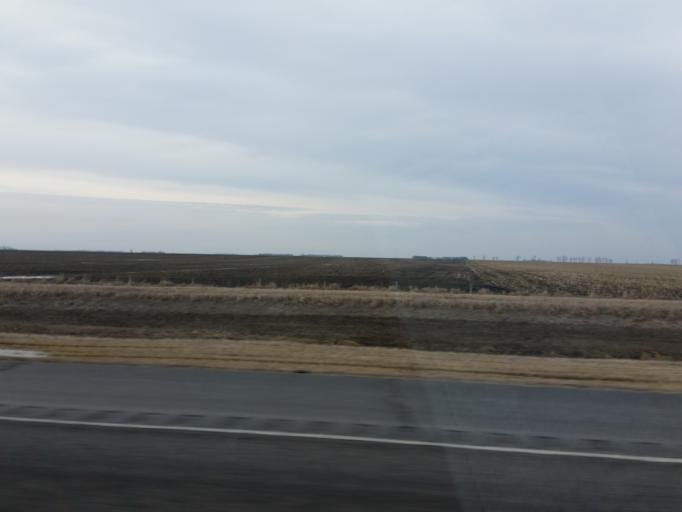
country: US
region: North Dakota
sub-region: Cass County
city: Casselton
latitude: 46.8767
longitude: -97.1228
